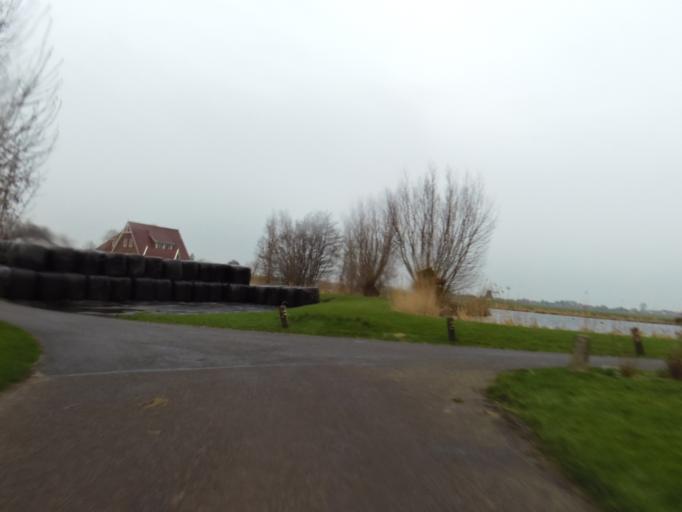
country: NL
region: South Holland
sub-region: Gemeente Leiderdorp
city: Leiderdorp
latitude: 52.1861
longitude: 4.5669
